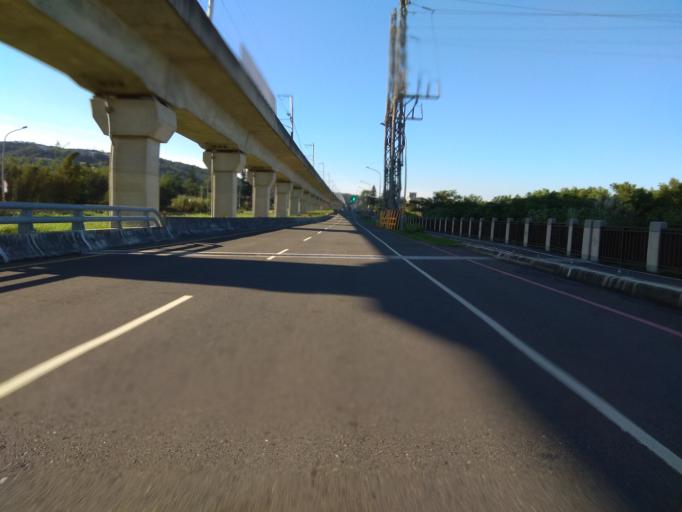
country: TW
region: Taiwan
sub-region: Hsinchu
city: Zhubei
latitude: 24.8877
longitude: 121.0730
